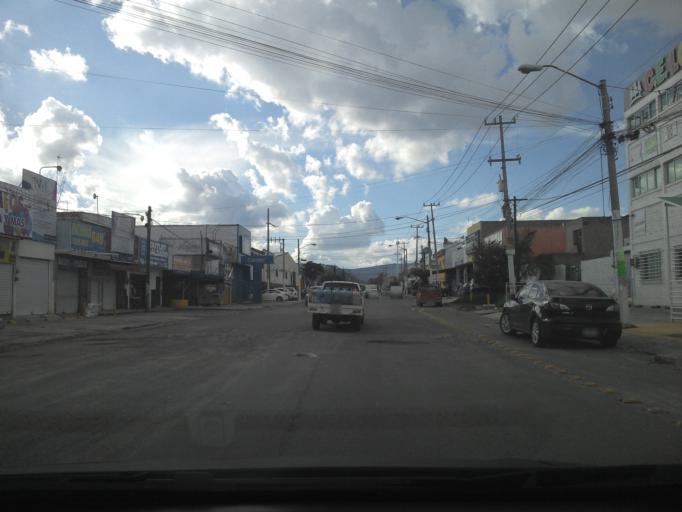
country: MX
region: Jalisco
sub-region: Tlajomulco de Zuniga
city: La Tijera
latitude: 20.6140
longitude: -103.4355
